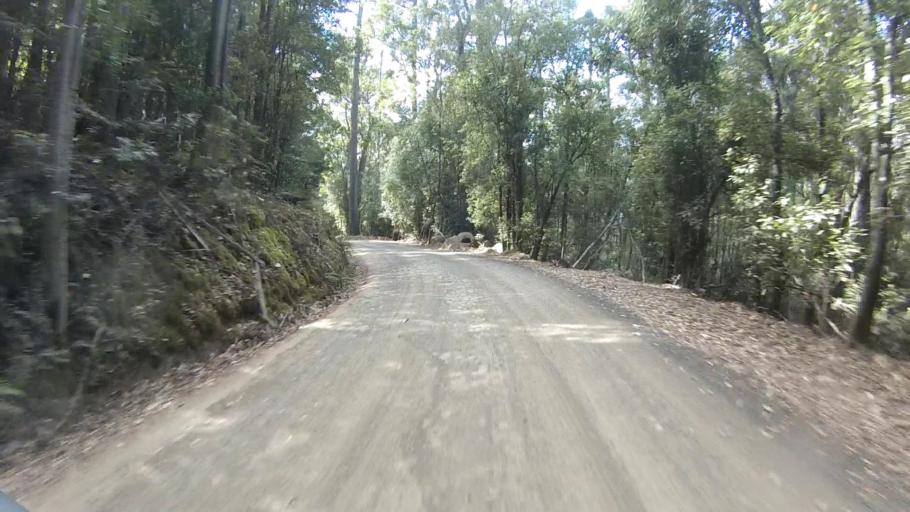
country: AU
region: Tasmania
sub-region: Derwent Valley
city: New Norfolk
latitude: -42.6763
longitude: 146.6960
